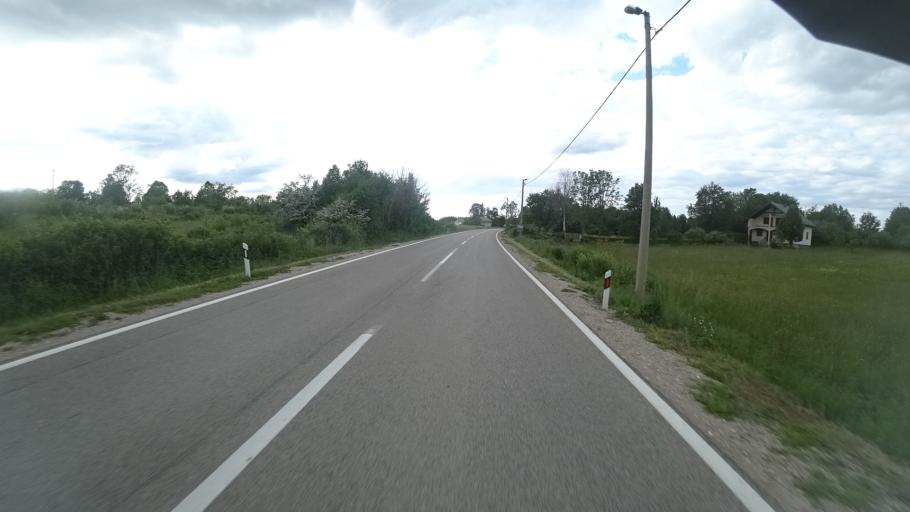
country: HR
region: Licko-Senjska
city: Gospic
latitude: 44.4894
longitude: 15.4627
